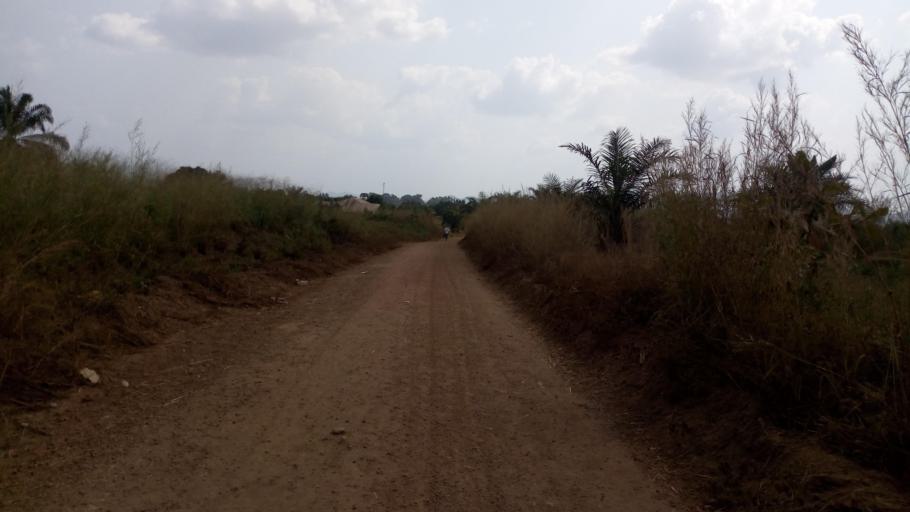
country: SL
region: Southern Province
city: Mogbwemo
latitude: 7.7778
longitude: -12.2985
